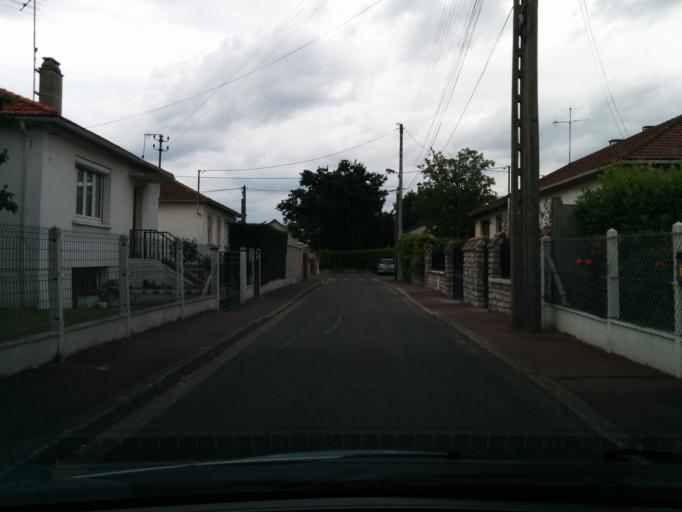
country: FR
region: Ile-de-France
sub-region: Departement des Yvelines
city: Aubergenville
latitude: 48.9715
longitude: 1.8516
